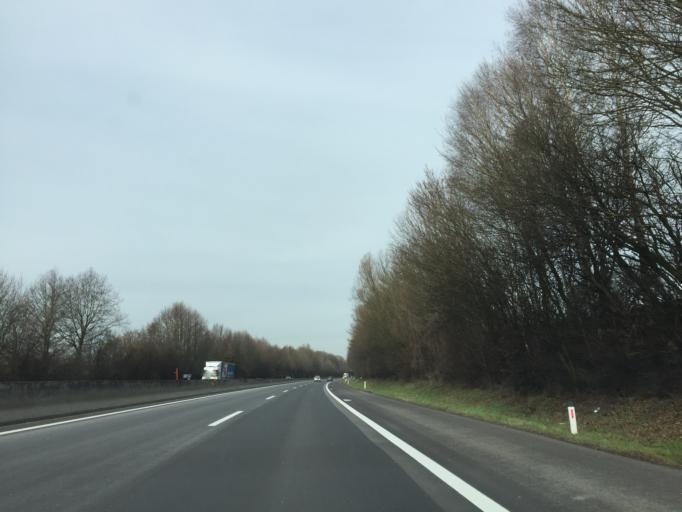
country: AT
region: Upper Austria
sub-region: Politischer Bezirk Scharding
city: Sankt Marienkirchen bei Schaerding
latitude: 48.3333
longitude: 13.4080
